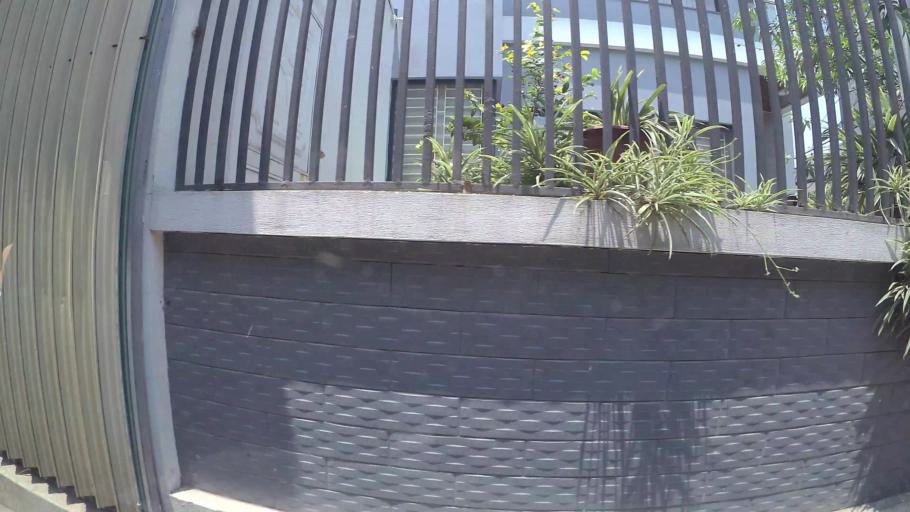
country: VN
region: Ha Noi
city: Hoan Kiem
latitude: 21.0240
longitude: 105.8922
